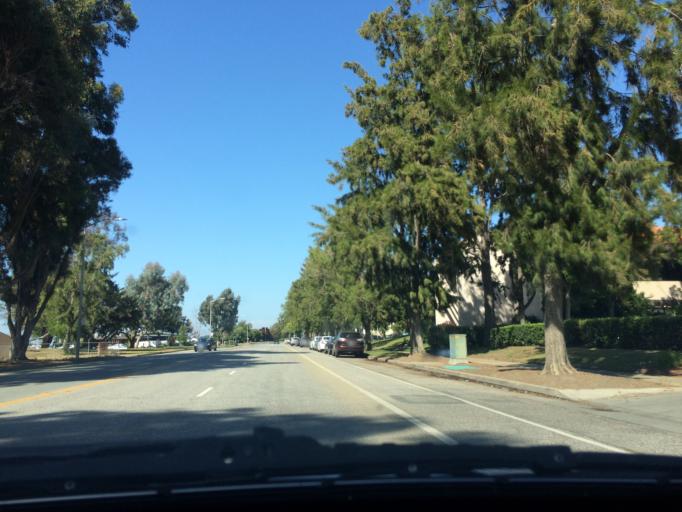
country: US
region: California
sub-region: Santa Clara County
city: Palo Alto
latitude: 37.4519
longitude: -122.1162
